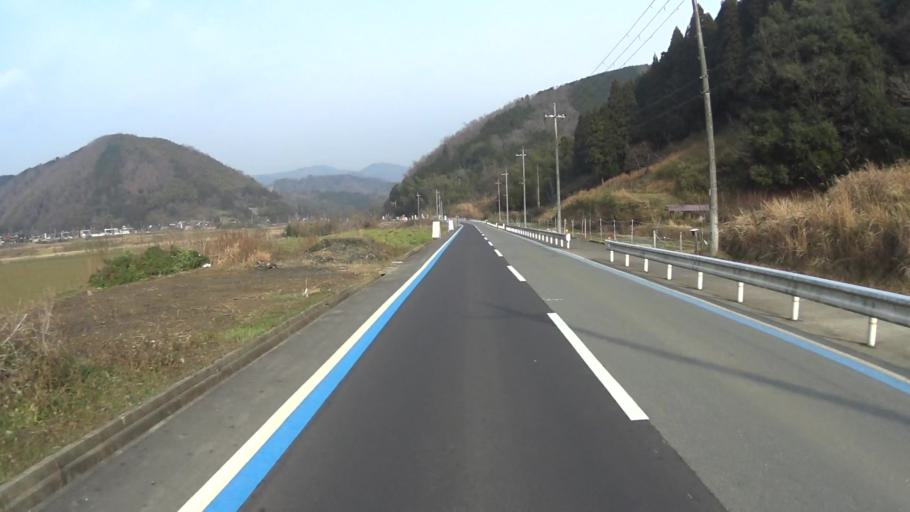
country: JP
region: Kyoto
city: Fukuchiyama
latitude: 35.3535
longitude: 135.1166
